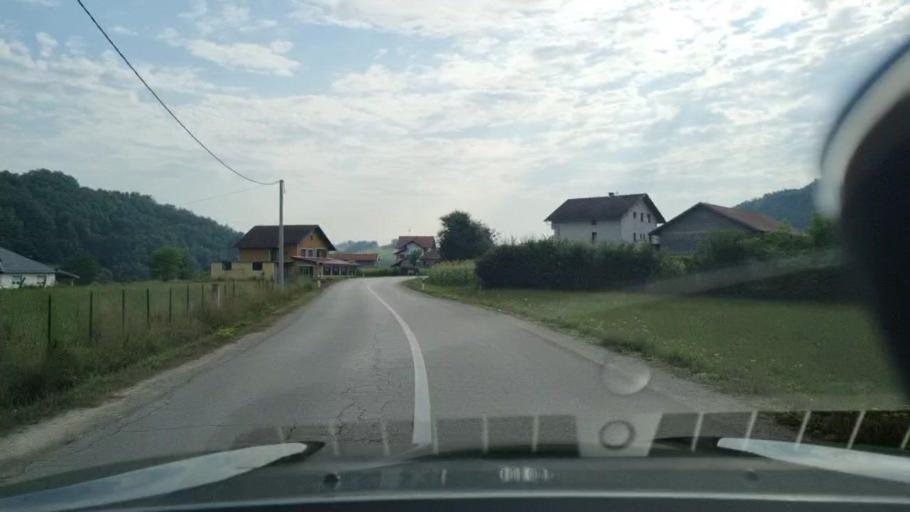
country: BA
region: Federation of Bosnia and Herzegovina
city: Vrnograc
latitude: 45.1621
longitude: 15.9727
